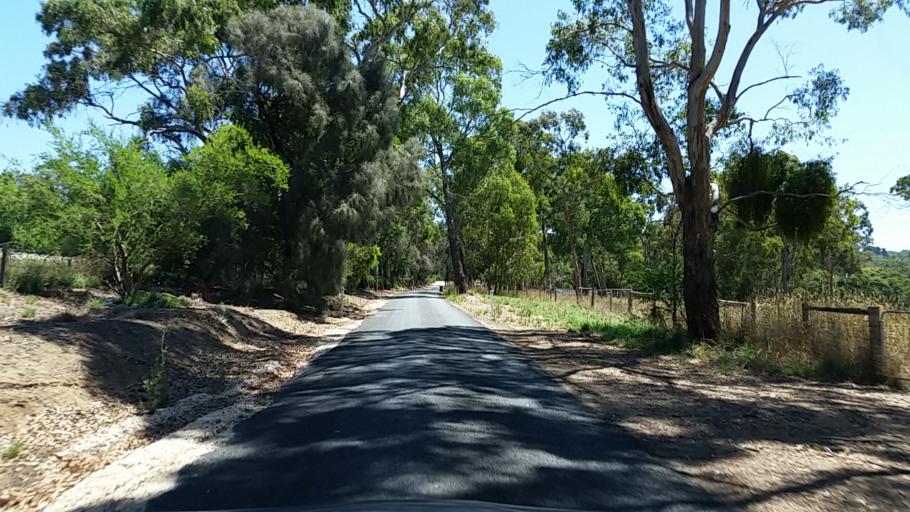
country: AU
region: South Australia
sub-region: Mount Barker
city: Little Hampton
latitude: -35.0368
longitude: 138.8592
